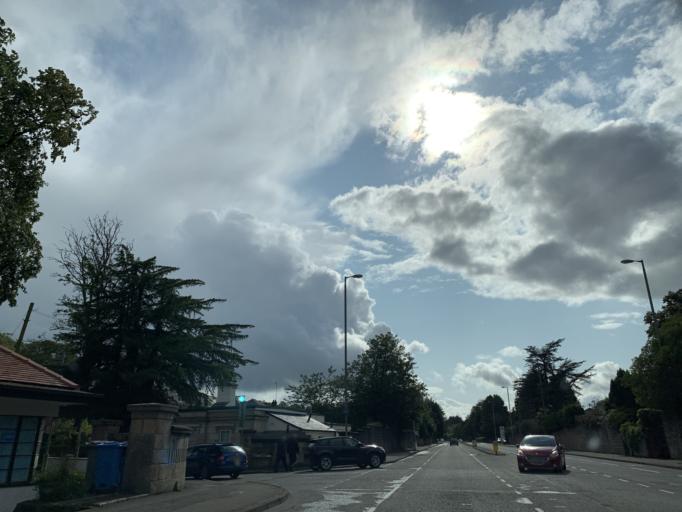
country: GB
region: Scotland
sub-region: East Renfrewshire
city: Newton Mearns
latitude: 55.7840
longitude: -4.3131
